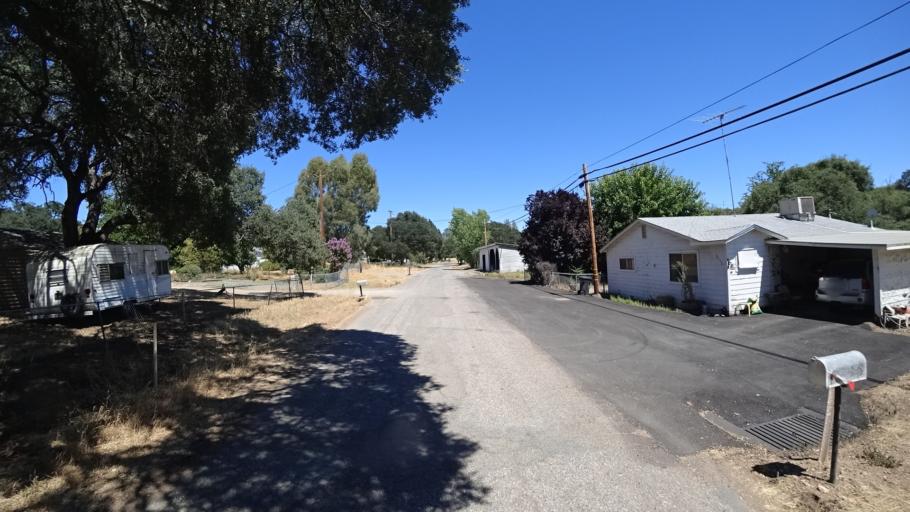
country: US
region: California
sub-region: Calaveras County
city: Valley Springs
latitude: 38.1858
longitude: -120.8695
